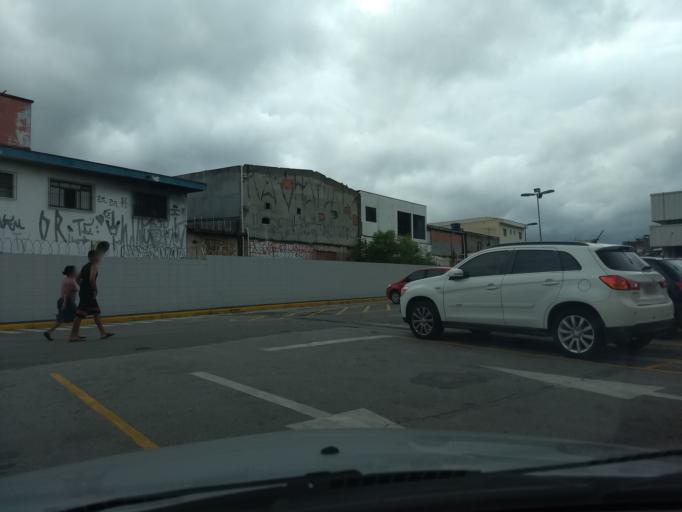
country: BR
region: Sao Paulo
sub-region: Osasco
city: Osasco
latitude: -23.5025
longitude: -46.7899
